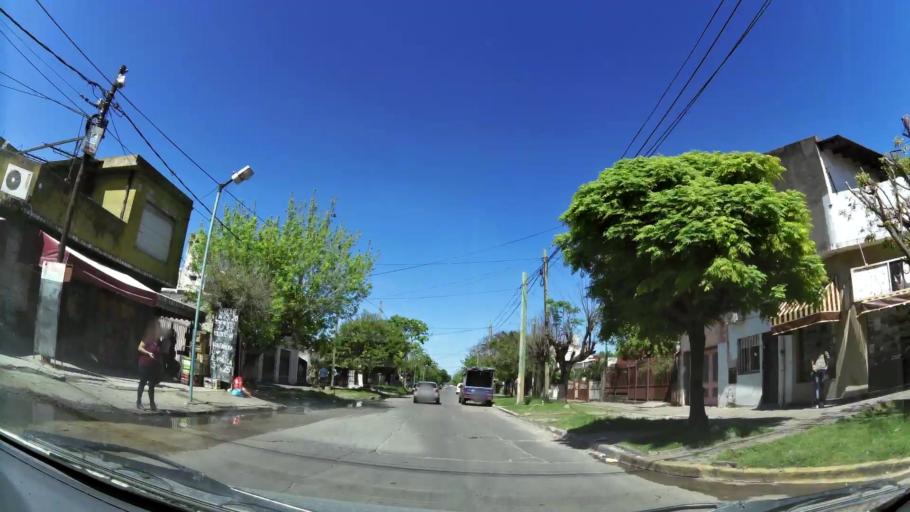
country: AR
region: Buenos Aires
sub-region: Partido de Quilmes
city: Quilmes
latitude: -34.7204
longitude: -58.3098
